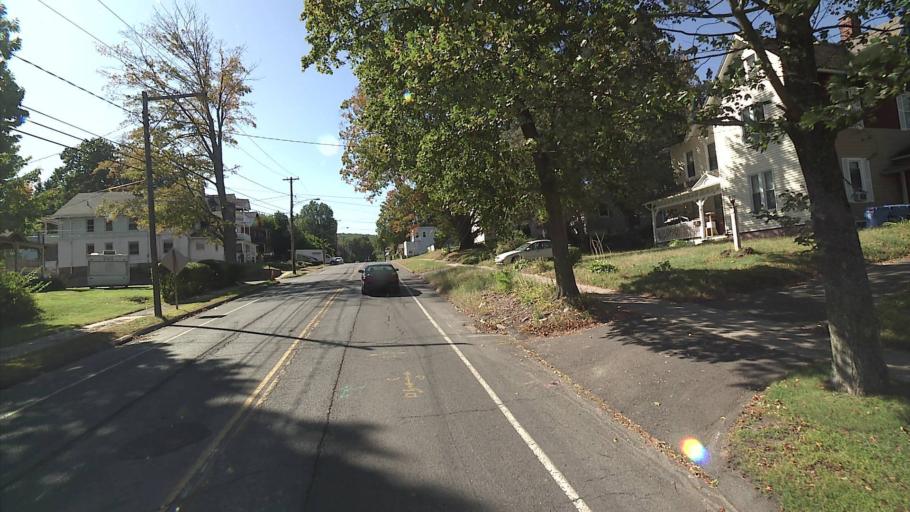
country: US
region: Connecticut
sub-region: Hartford County
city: Bristol
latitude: 41.6662
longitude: -72.9478
